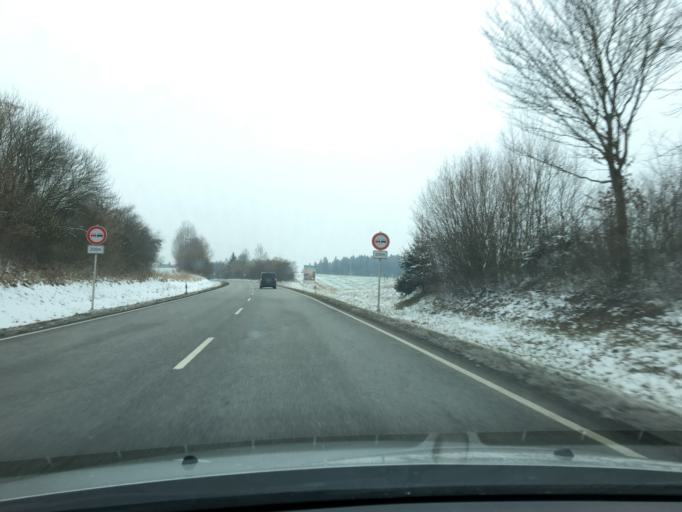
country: DE
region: Bavaria
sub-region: Lower Bavaria
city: Furth
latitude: 48.4282
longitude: 12.3975
